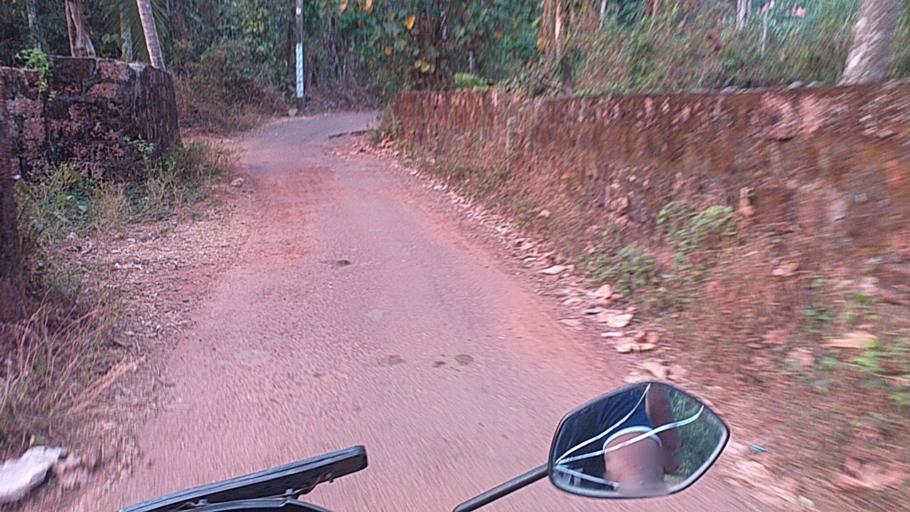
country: IN
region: Kerala
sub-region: Thrissur District
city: Kunnamkulam
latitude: 10.7388
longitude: 76.0409
